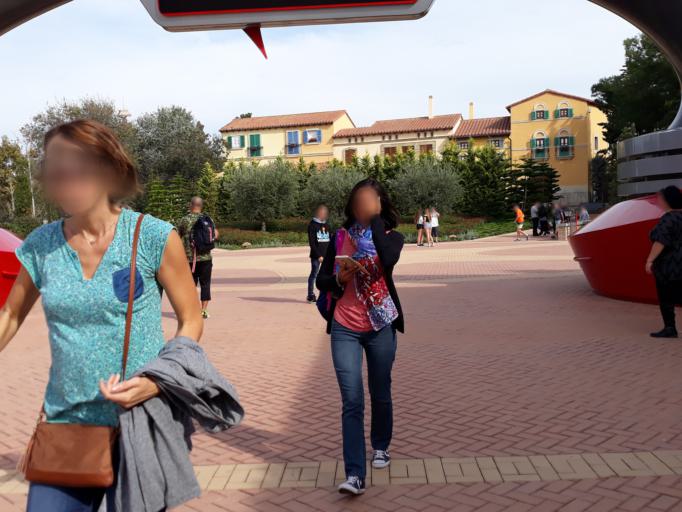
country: ES
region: Catalonia
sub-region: Provincia de Tarragona
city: Salou
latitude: 41.0856
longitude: 1.1530
